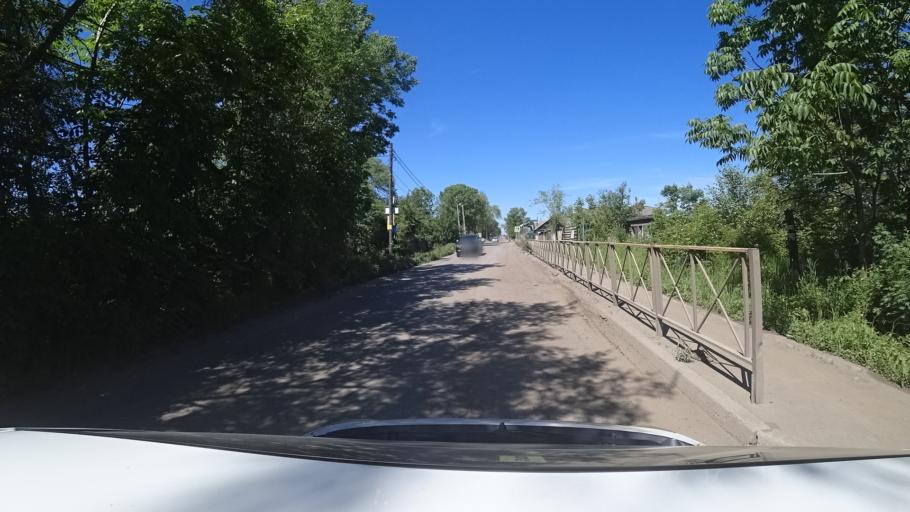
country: RU
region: Khabarovsk Krai
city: Topolevo
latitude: 48.4714
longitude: 135.1788
